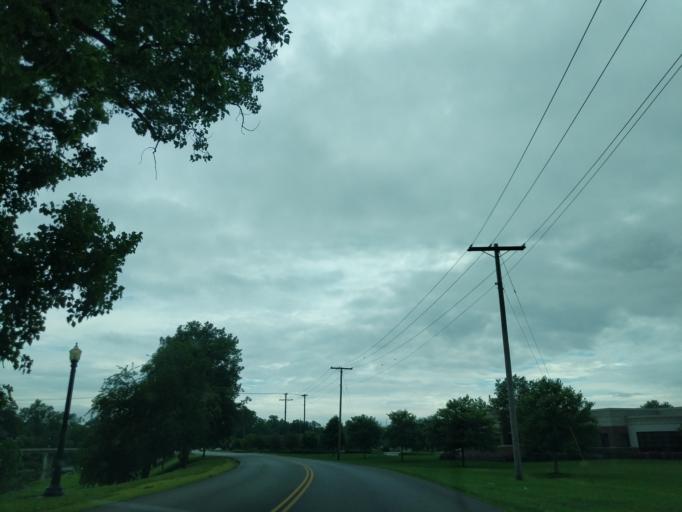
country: US
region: Indiana
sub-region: Delaware County
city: Muncie
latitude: 40.1951
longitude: -85.3972
